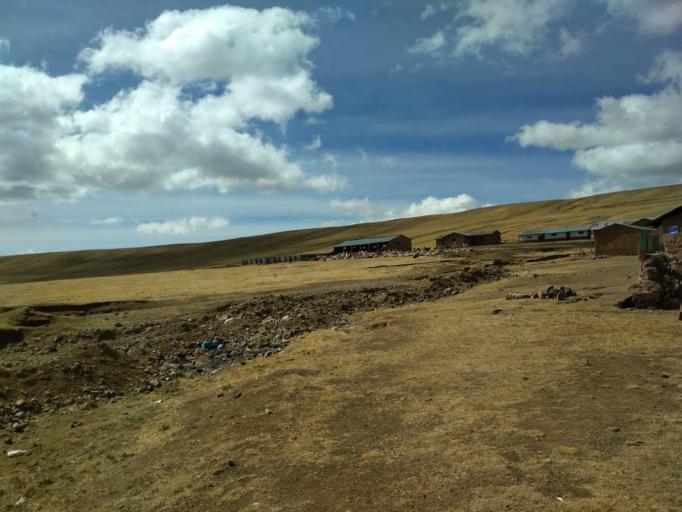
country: PE
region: Huancavelica
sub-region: Provincia de Huancavelica
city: Acobambilla
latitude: -12.7251
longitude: -75.5076
